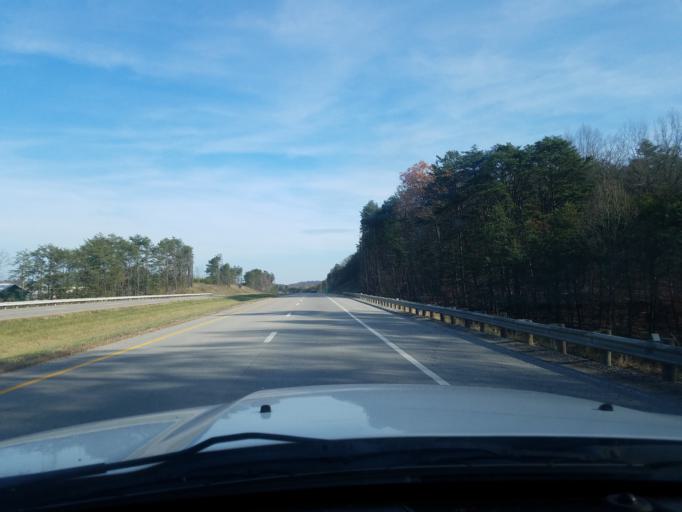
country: US
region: West Virginia
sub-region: Wood County
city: Washington
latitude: 39.2364
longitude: -81.7567
